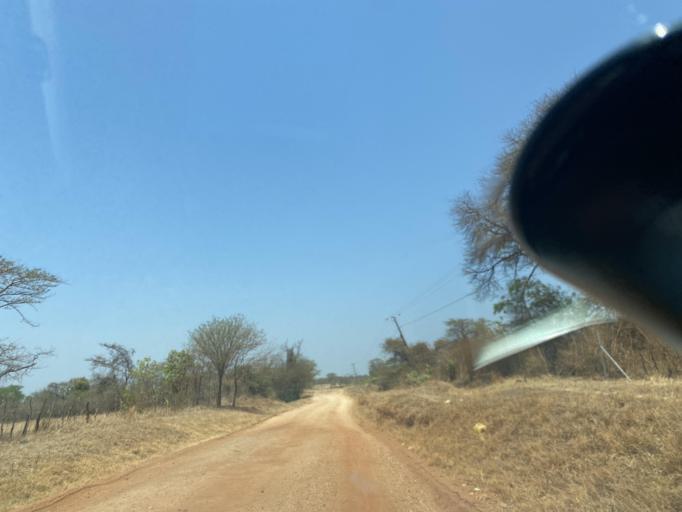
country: ZM
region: Lusaka
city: Lusaka
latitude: -15.5388
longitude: 28.0806
